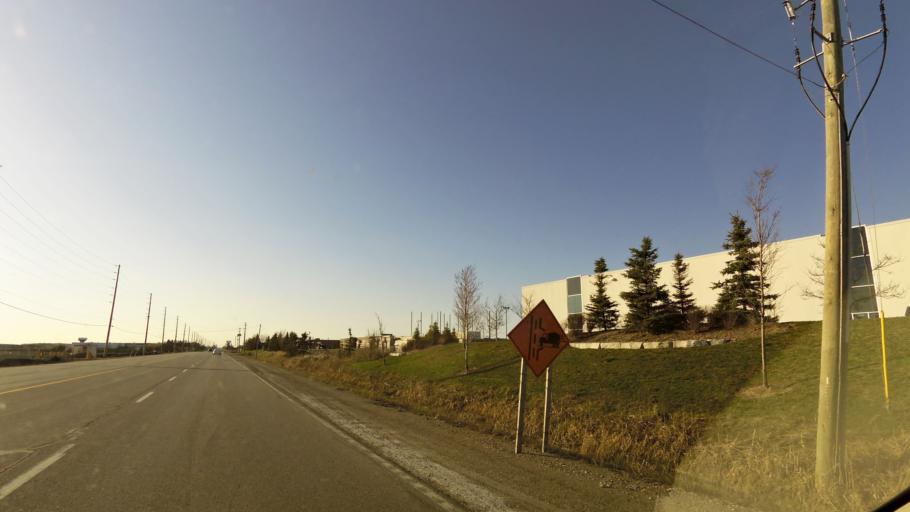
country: CA
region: Ontario
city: Brampton
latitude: 43.8501
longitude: -79.7211
